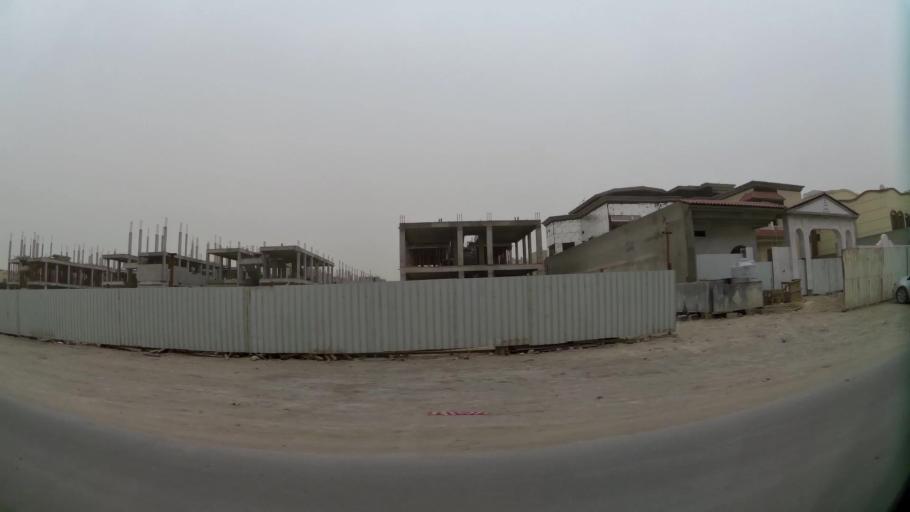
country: QA
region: Baladiyat ad Dawhah
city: Doha
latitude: 25.2460
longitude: 51.4860
